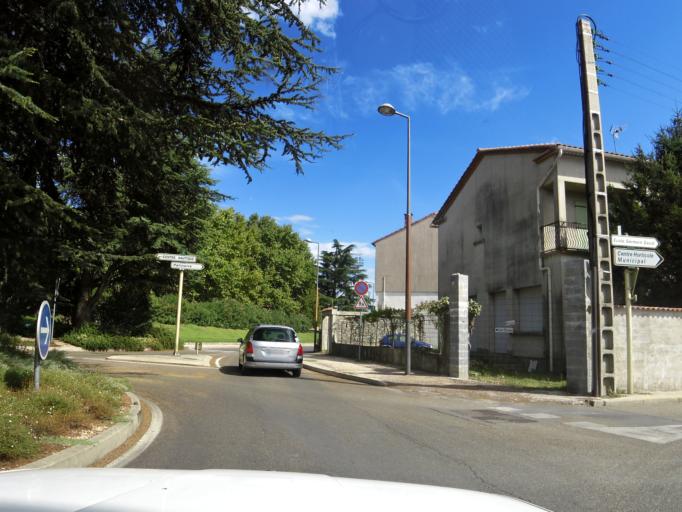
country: FR
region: Languedoc-Roussillon
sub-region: Departement du Gard
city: Ales
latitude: 44.1197
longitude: 4.0867
